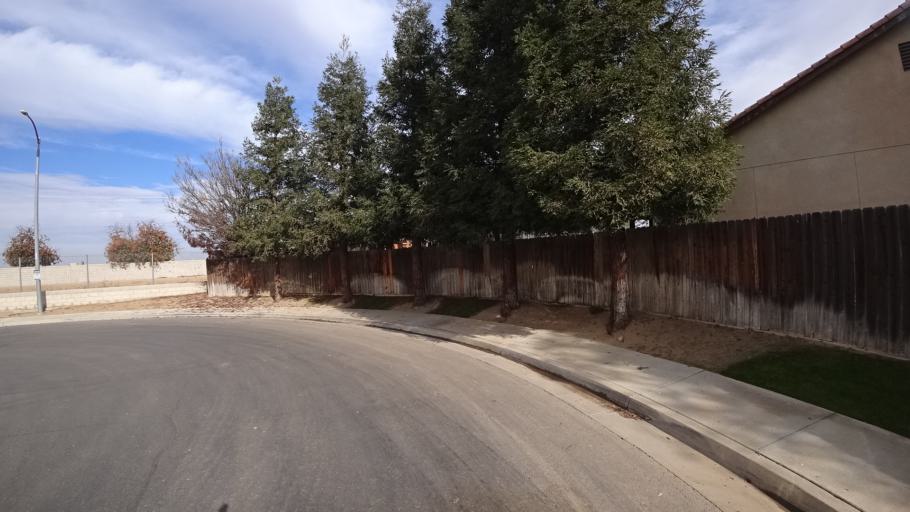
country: US
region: California
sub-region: Kern County
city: Rosedale
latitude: 35.4264
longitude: -119.1444
